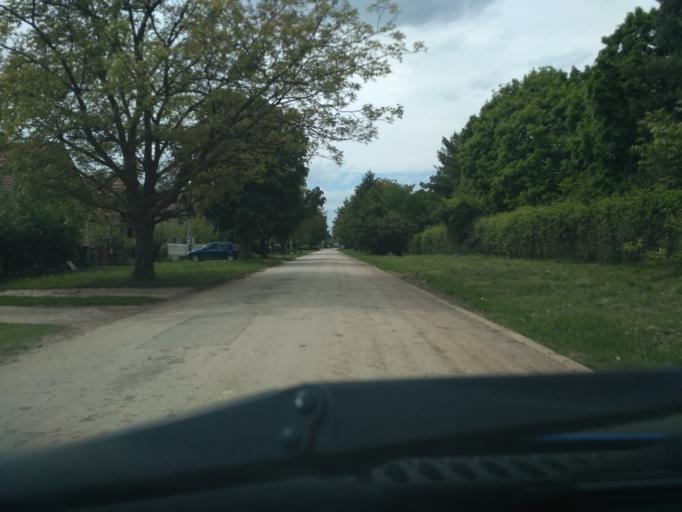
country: RS
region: Central Serbia
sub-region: Pomoravski Okrug
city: Svilajnac
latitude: 44.2258
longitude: 21.2090
